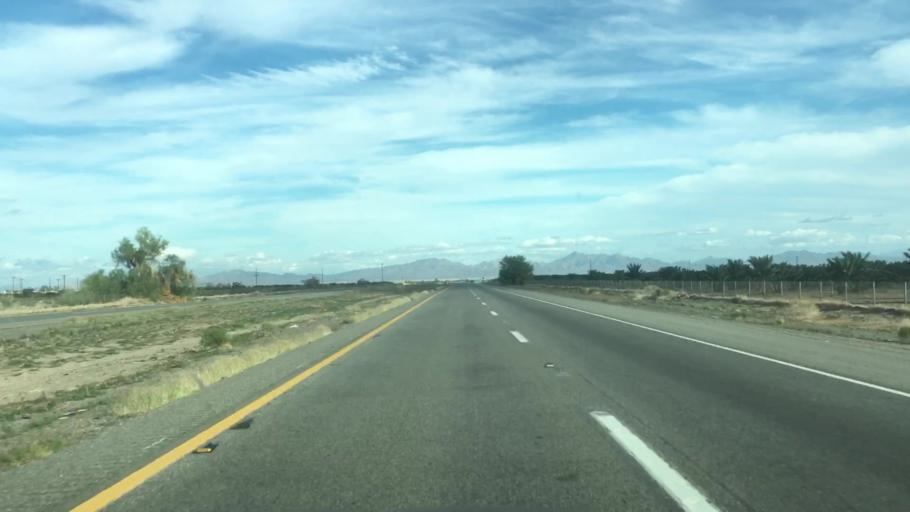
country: US
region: California
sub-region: Riverside County
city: Mesa Verde
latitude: 33.6066
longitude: -114.6883
